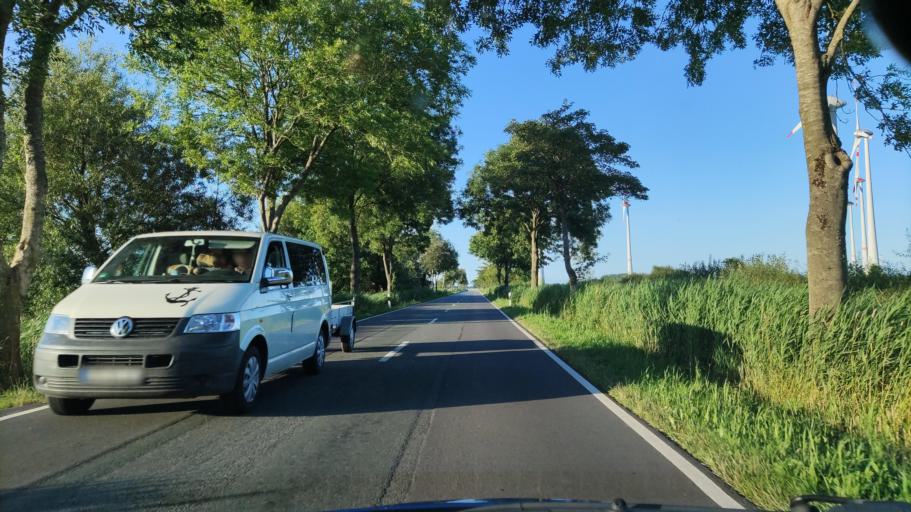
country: DE
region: Lower Saxony
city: Wittmund
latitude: 53.5864
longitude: 7.8005
